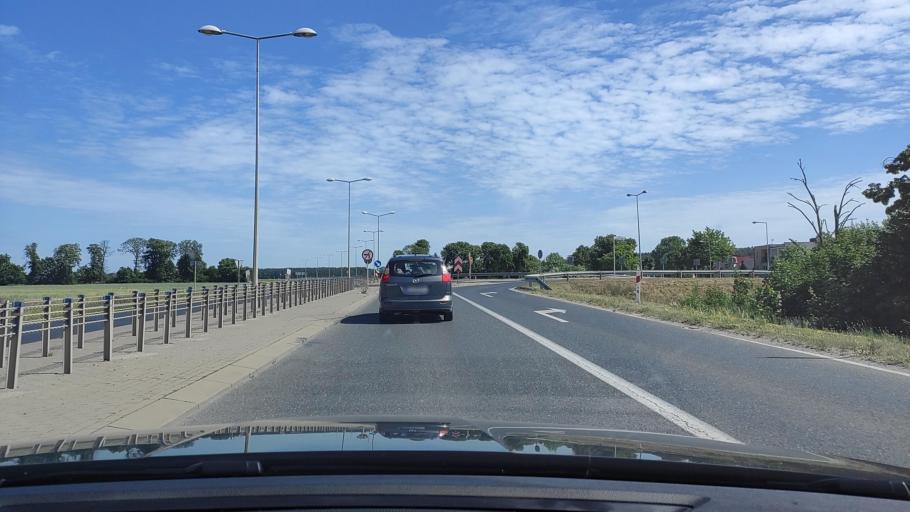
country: PL
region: Greater Poland Voivodeship
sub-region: Powiat poznanski
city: Murowana Goslina
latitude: 52.5467
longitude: 16.9896
